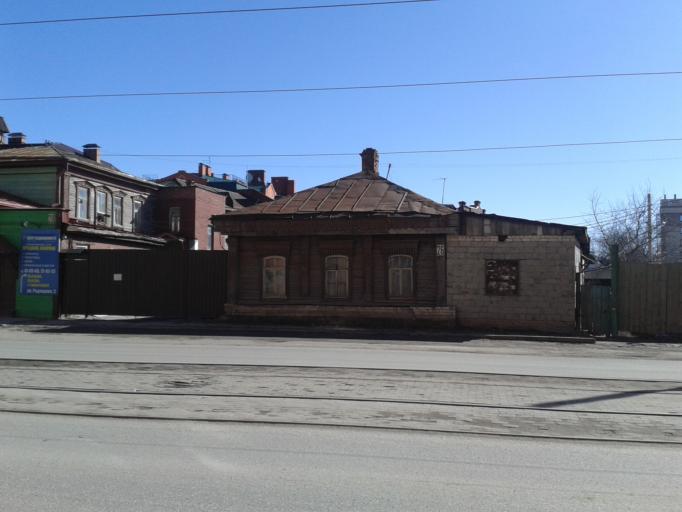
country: RU
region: Ulyanovsk
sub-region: Ulyanovskiy Rayon
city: Ulyanovsk
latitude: 54.3238
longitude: 48.4046
